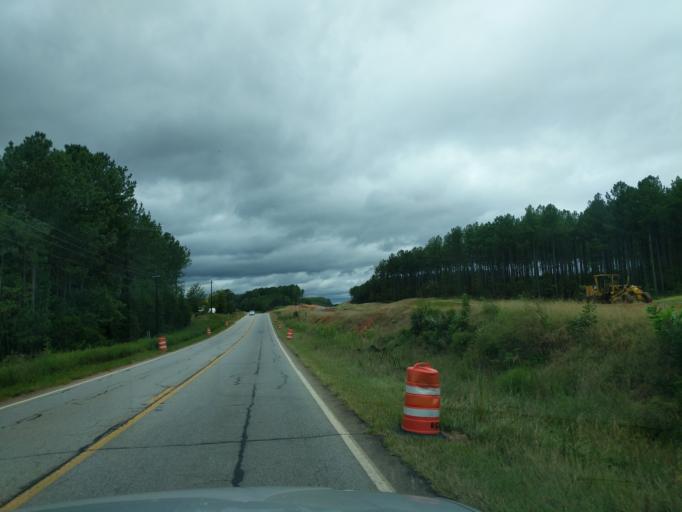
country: US
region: Georgia
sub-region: Wilkes County
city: Washington
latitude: 33.6818
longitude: -82.6349
